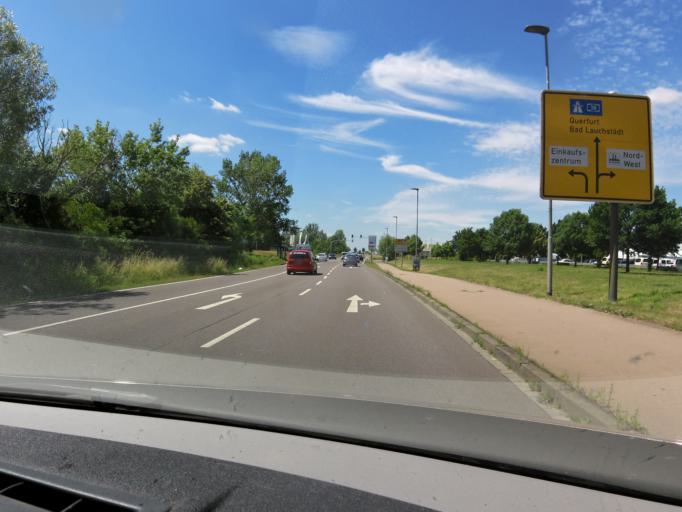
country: DE
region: Saxony-Anhalt
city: Merseburg
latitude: 51.3725
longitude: 11.9768
